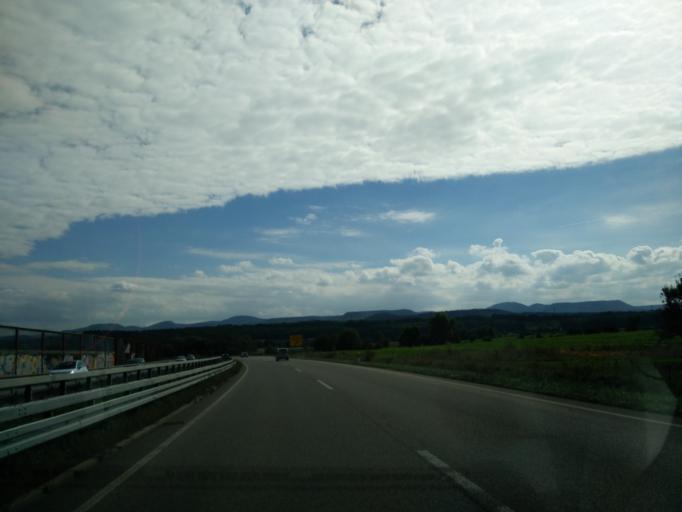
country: DE
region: Baden-Wuerttemberg
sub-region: Tuebingen Region
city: Kusterdingen
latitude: 48.5003
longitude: 9.1241
